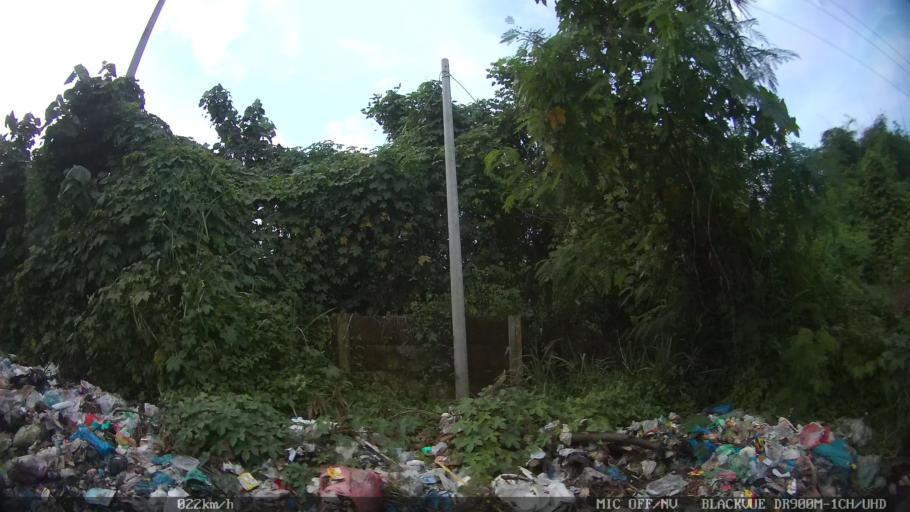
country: ID
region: North Sumatra
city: Medan
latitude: 3.6057
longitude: 98.7309
